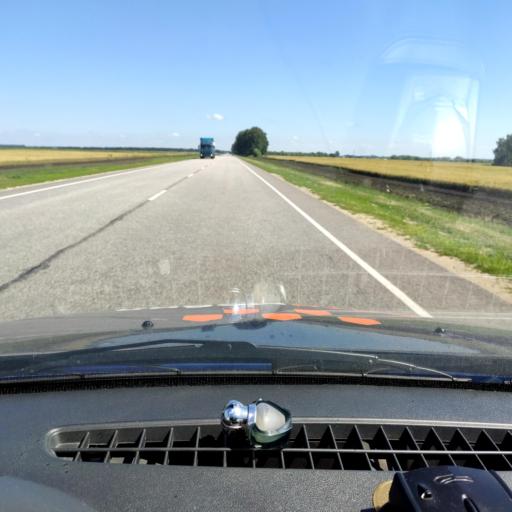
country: RU
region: Orjol
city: Pokrovskoye
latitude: 52.6355
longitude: 36.6881
